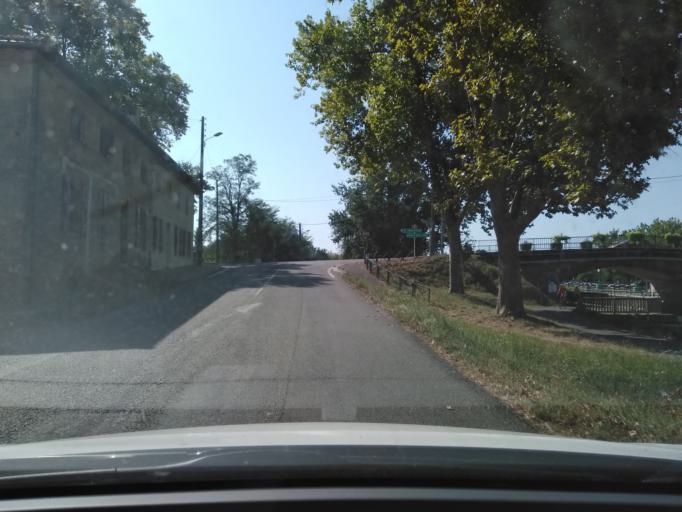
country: FR
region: Midi-Pyrenees
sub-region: Departement du Tarn-et-Garonne
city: Montech
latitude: 43.9602
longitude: 1.2375
